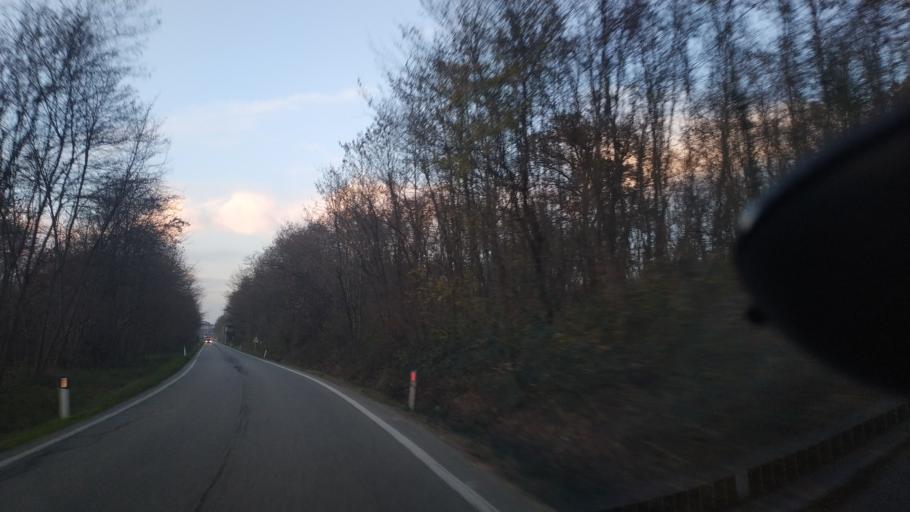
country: IT
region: Piedmont
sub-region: Provincia di Torino
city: Foglizzo
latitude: 45.2634
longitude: 7.8285
